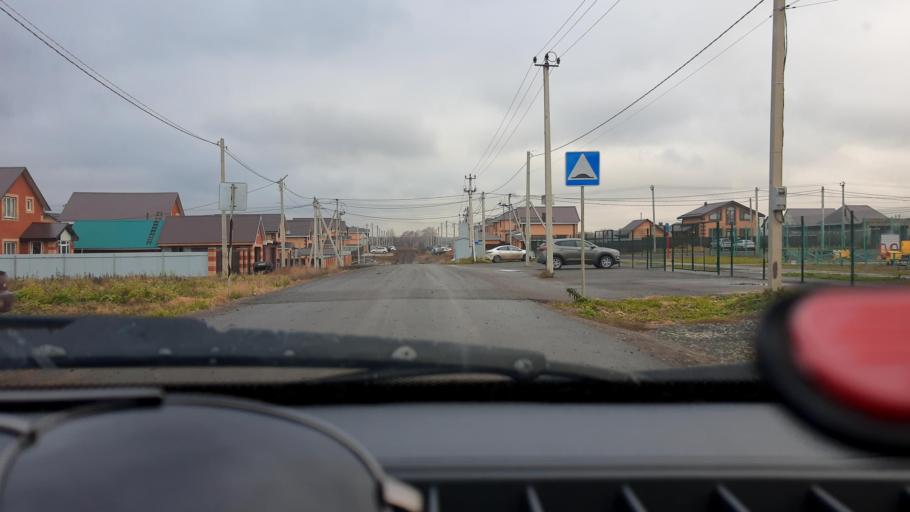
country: RU
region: Bashkortostan
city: Ufa
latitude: 54.6087
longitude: 55.9122
